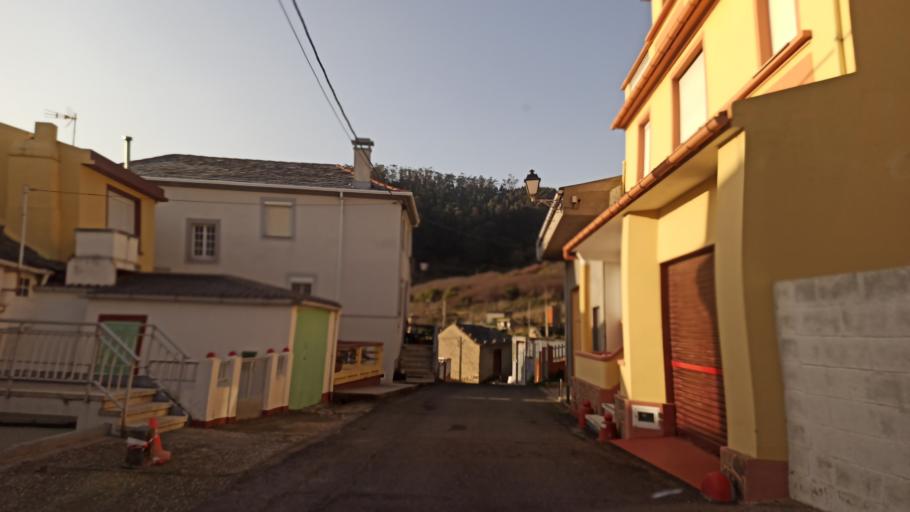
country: ES
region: Galicia
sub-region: Provincia de Lugo
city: Viveiro
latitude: 43.7730
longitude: -7.6687
